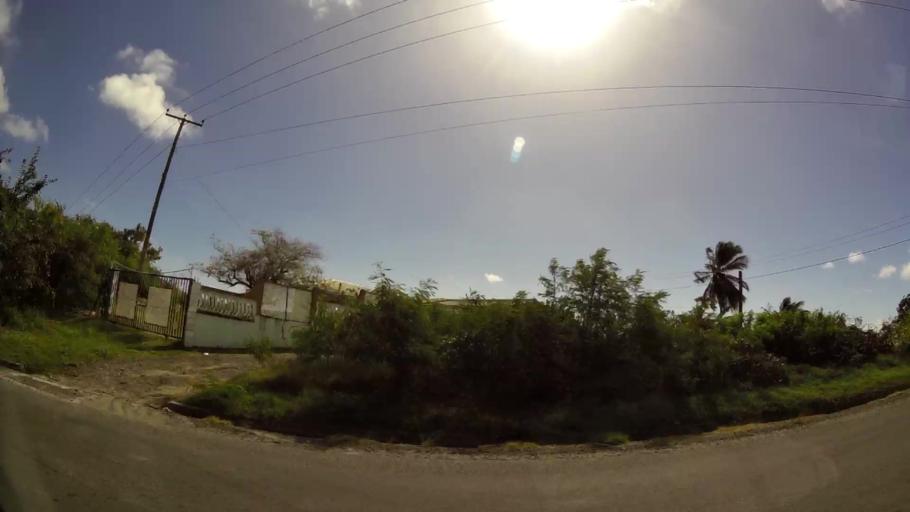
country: LC
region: Laborie Quarter
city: Laborie
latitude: 13.7439
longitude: -60.9802
